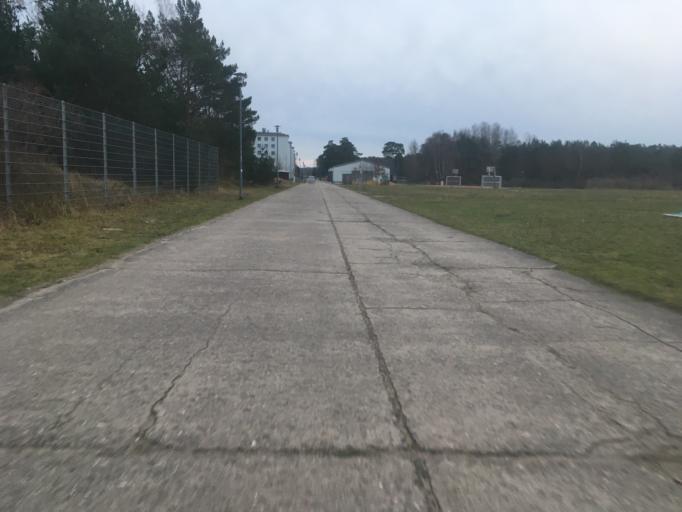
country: DE
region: Mecklenburg-Vorpommern
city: Ostseebad Binz
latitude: 54.4534
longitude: 13.5685
